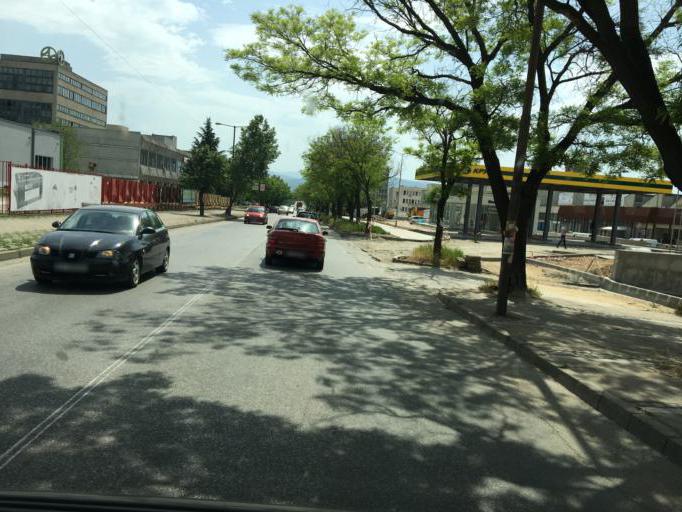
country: BG
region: Blagoevgrad
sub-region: Obshtina Blagoevgrad
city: Blagoevgrad
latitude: 42.0091
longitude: 23.0869
